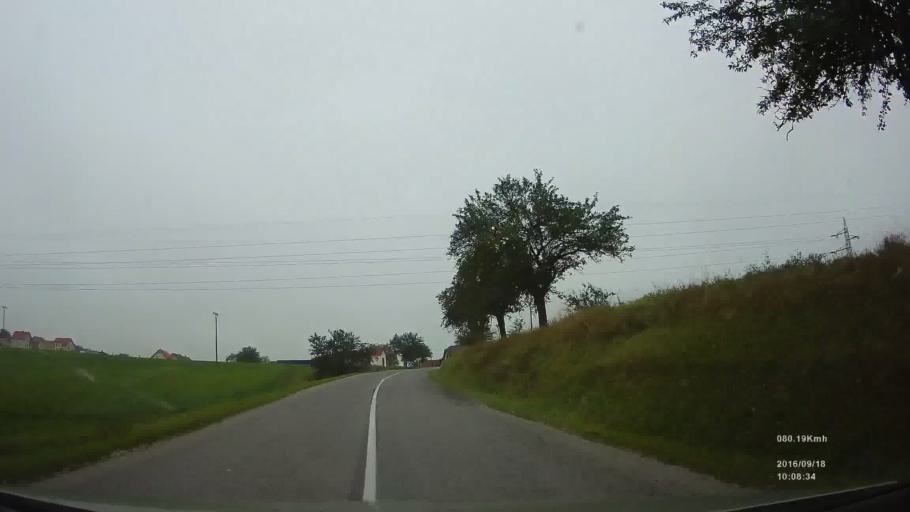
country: SK
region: Kosicky
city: Spisska Nova Ves
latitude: 48.9491
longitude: 20.6608
